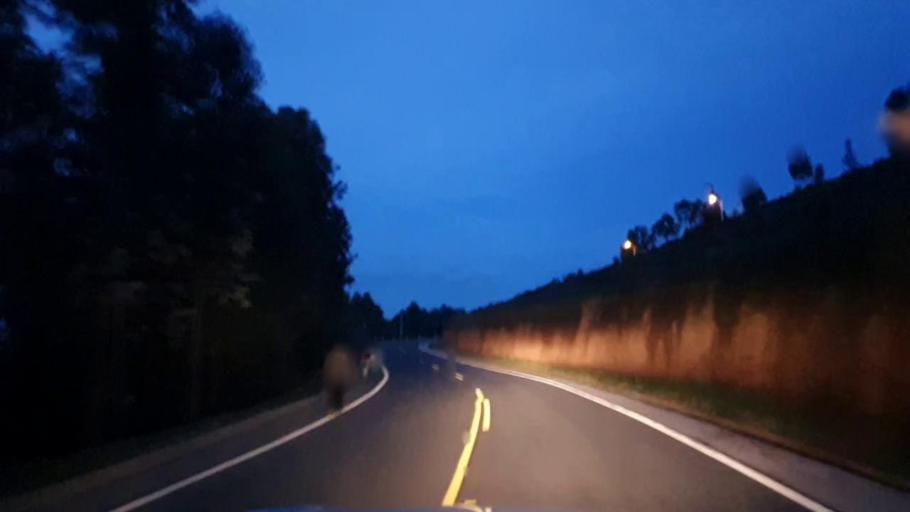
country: RW
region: Southern Province
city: Gikongoro
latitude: -2.4667
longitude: 29.5719
